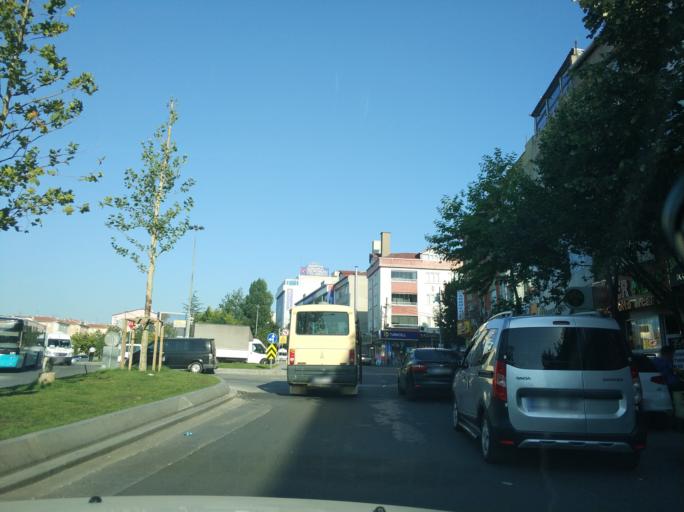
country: TR
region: Istanbul
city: Sultangazi
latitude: 41.0822
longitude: 28.9155
